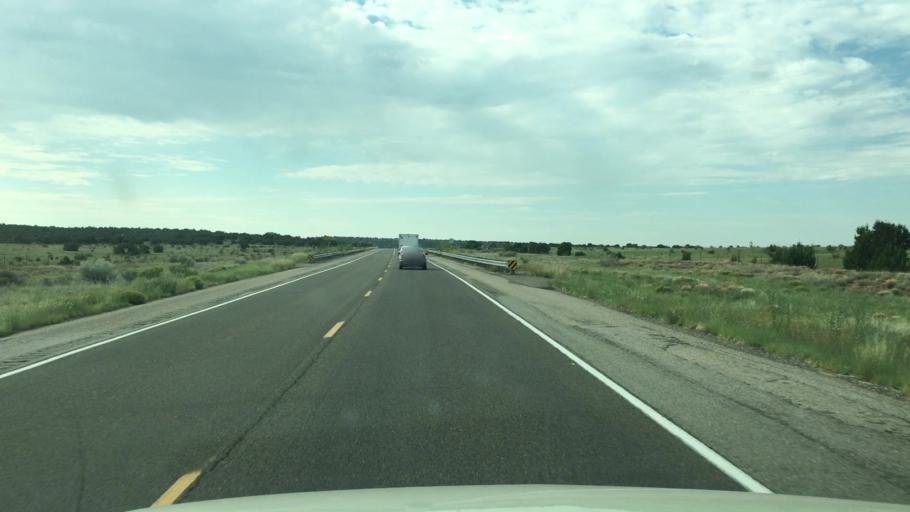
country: US
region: New Mexico
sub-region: Santa Fe County
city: Eldorado at Santa Fe
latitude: 35.2934
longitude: -105.8255
